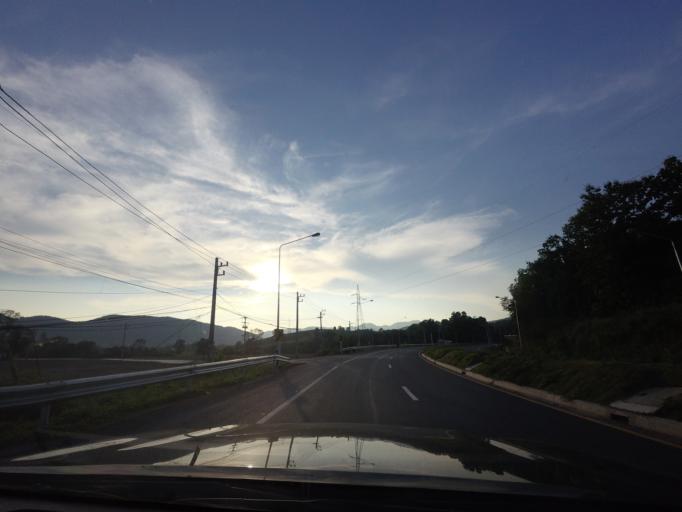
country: TH
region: Nan
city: Wiang Sa
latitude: 18.5220
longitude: 100.5770
